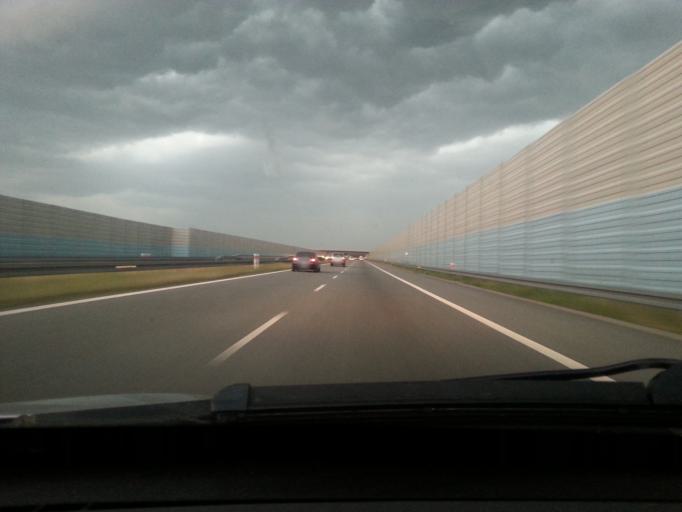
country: PL
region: Lodz Voivodeship
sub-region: powiat Lowicki
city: Lyszkowice
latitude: 51.9804
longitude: 19.8831
